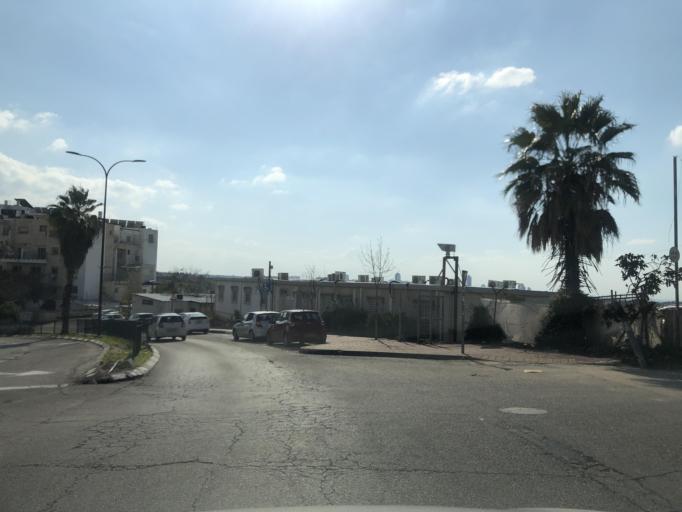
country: IL
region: Jerusalem
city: Modiin Ilit
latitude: 31.9387
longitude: 35.0361
